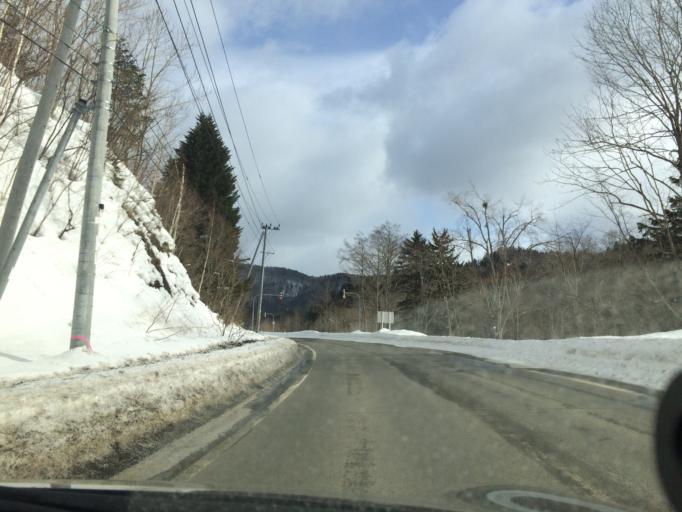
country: JP
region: Hokkaido
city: Shimo-furano
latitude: 43.0441
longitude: 142.5191
